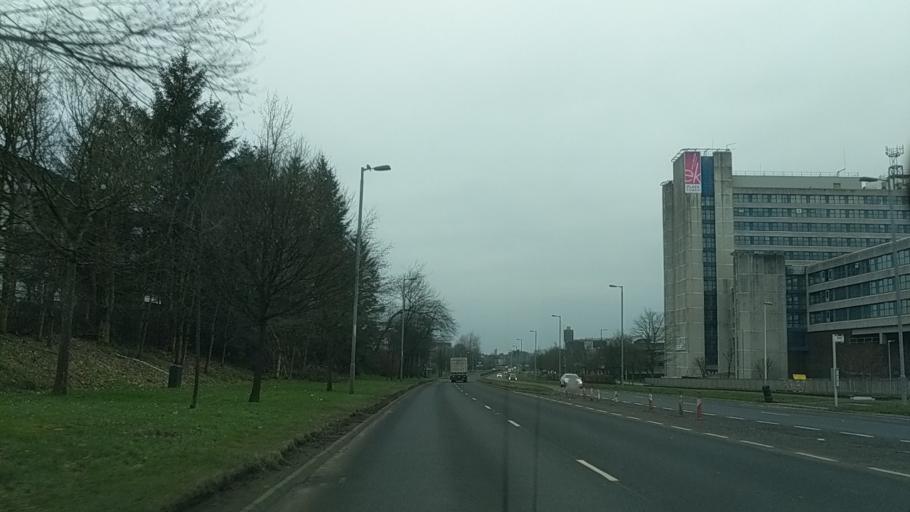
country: GB
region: Scotland
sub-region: South Lanarkshire
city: East Kilbride
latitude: 55.7588
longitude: -4.1775
